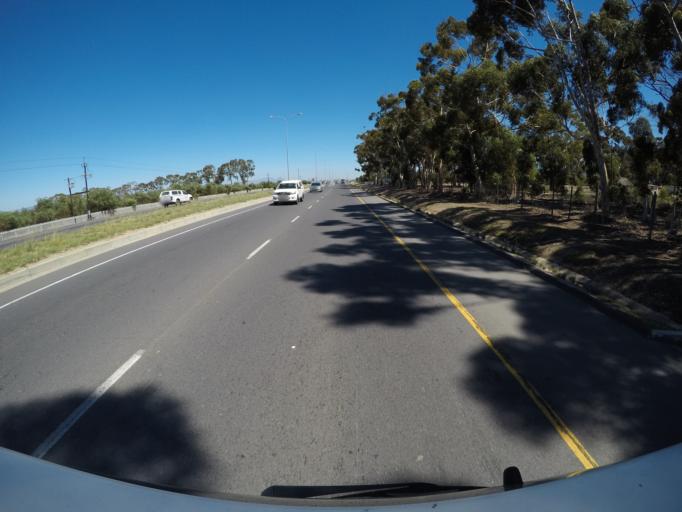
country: ZA
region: Western Cape
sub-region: Overberg District Municipality
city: Grabouw
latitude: -34.1156
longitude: 18.8734
